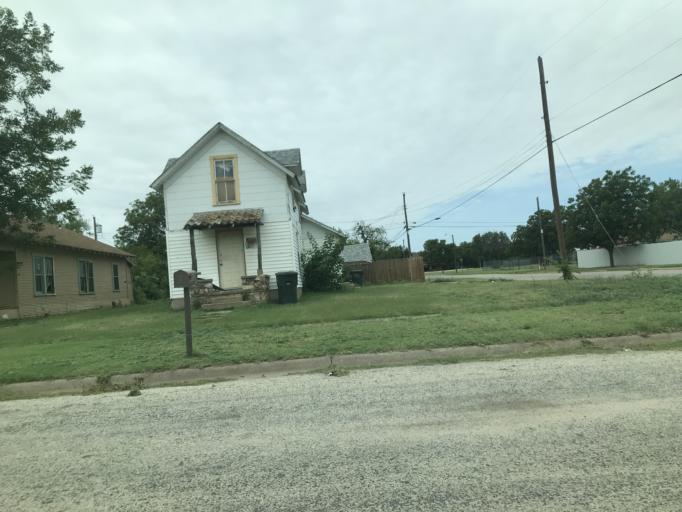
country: US
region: Texas
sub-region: Taylor County
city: Abilene
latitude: 32.4405
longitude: -99.7358
